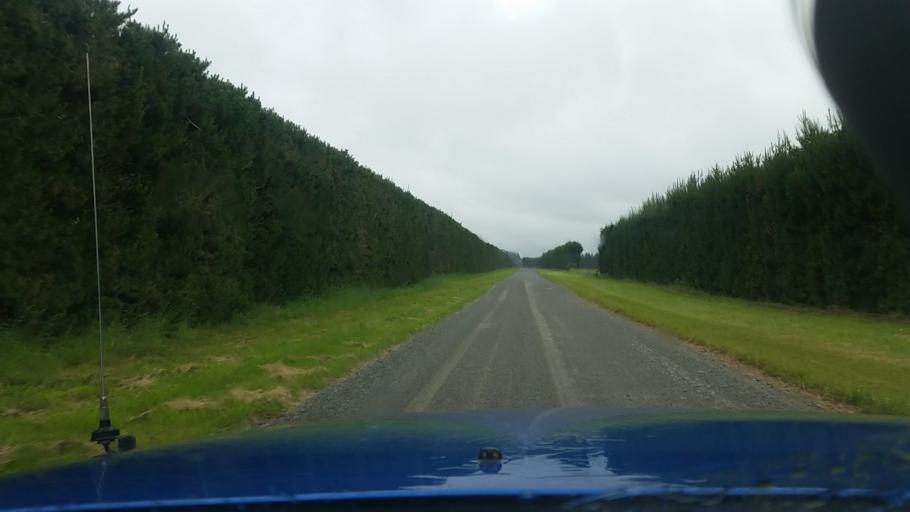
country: NZ
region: Canterbury
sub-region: Ashburton District
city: Tinwald
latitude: -43.9067
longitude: 171.5509
